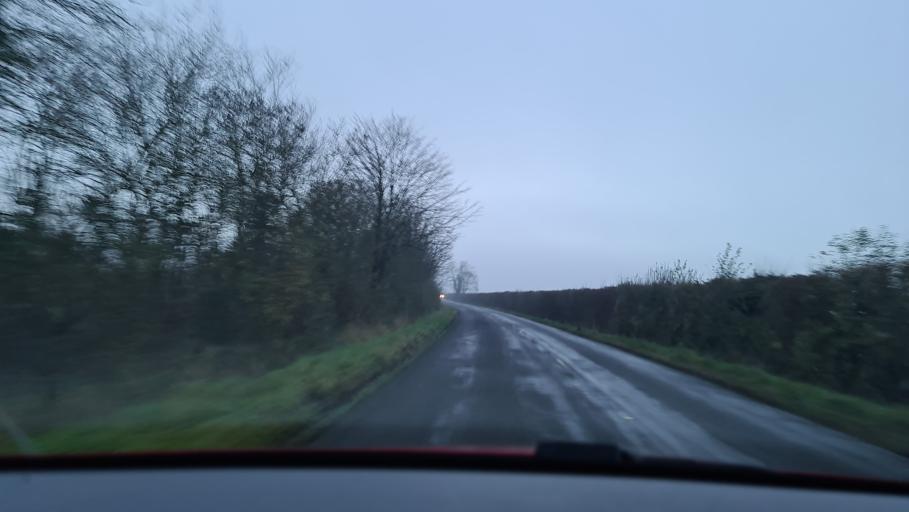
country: GB
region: England
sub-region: Oxfordshire
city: Bicester
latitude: 51.8951
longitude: -1.2141
